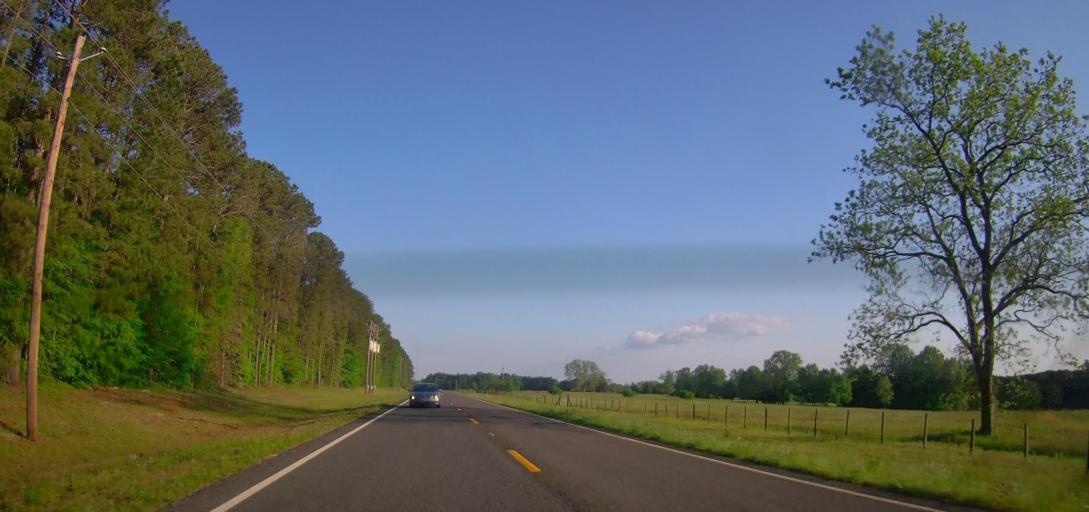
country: US
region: Georgia
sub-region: Jasper County
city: Monticello
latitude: 33.4545
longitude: -83.6307
